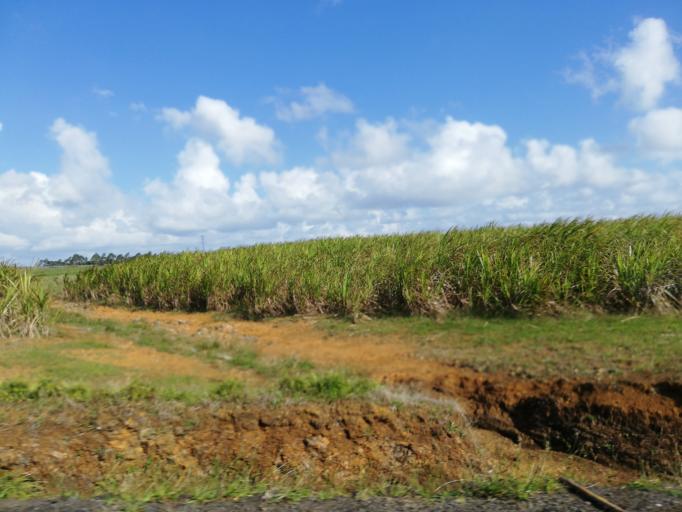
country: MU
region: Moka
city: Verdun
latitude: -20.2248
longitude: 57.5516
